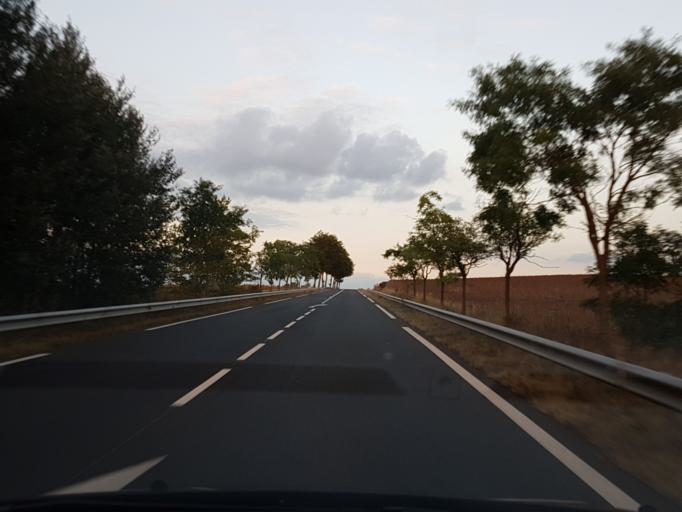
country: FR
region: Languedoc-Roussillon
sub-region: Departement de l'Aude
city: Saint-Martin-Lalande
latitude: 43.1713
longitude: 2.0029
